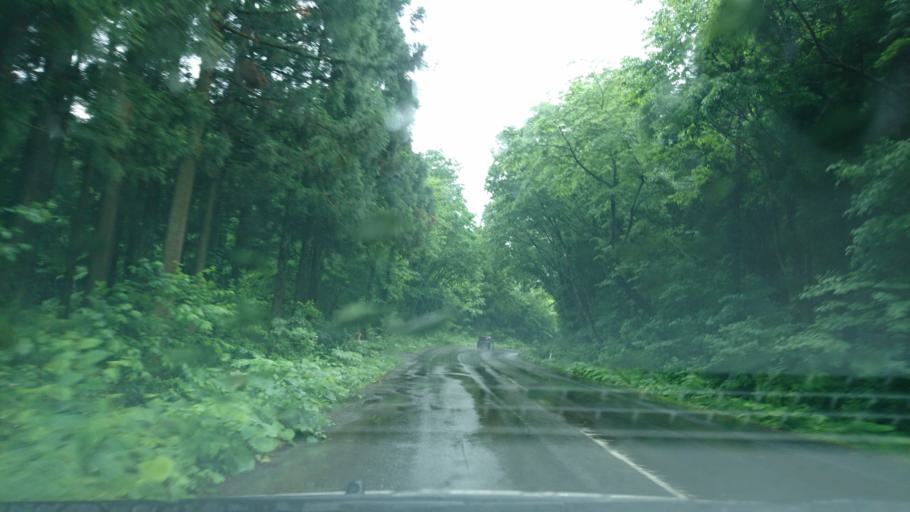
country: JP
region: Iwate
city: Ichinoseki
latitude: 39.0113
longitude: 140.8891
